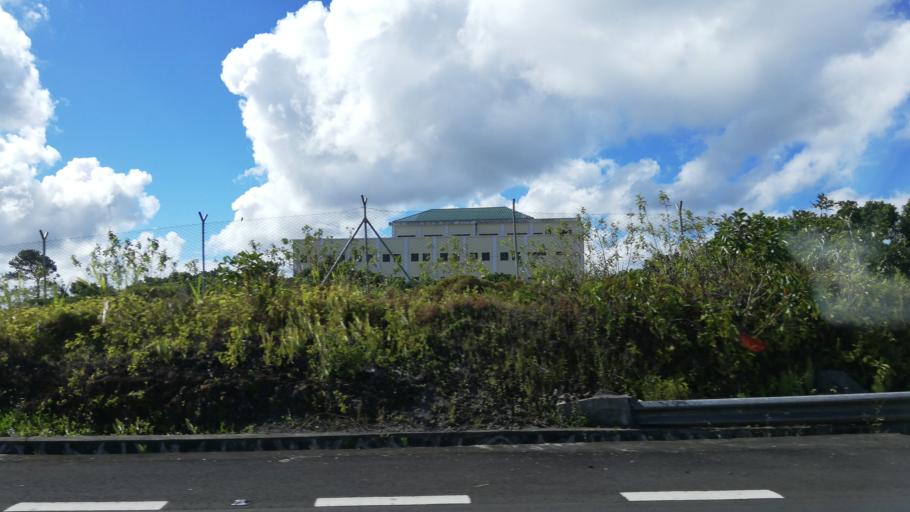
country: MU
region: Moka
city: Quartier Militaire
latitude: -20.2517
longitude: 57.5856
